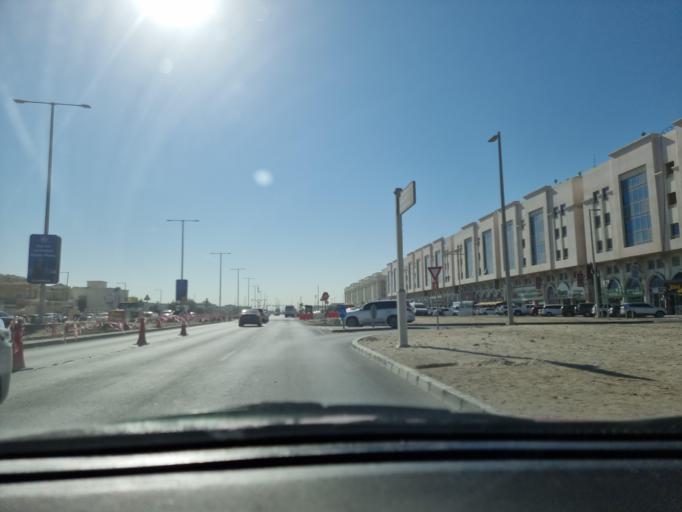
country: AE
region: Abu Dhabi
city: Abu Dhabi
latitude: 24.4227
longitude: 54.5656
